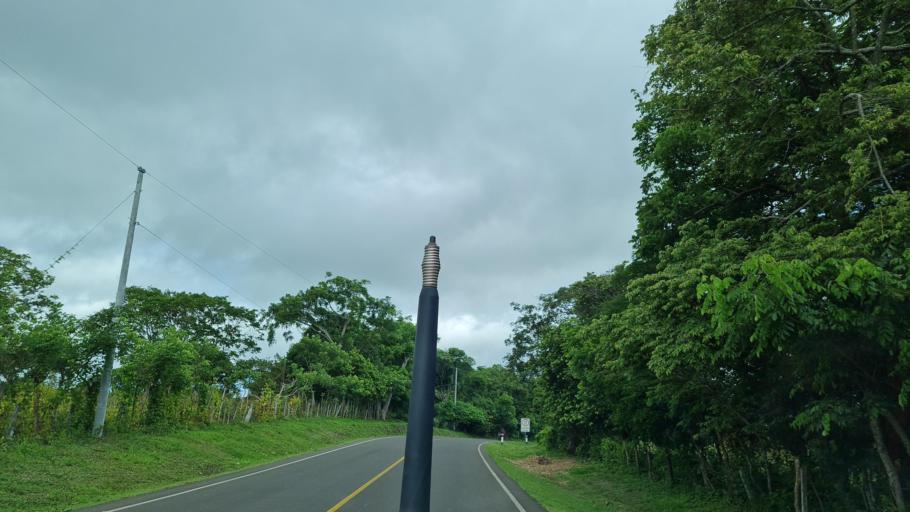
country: NI
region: Boaco
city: San Jose de los Remates
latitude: 12.5962
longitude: -85.8991
